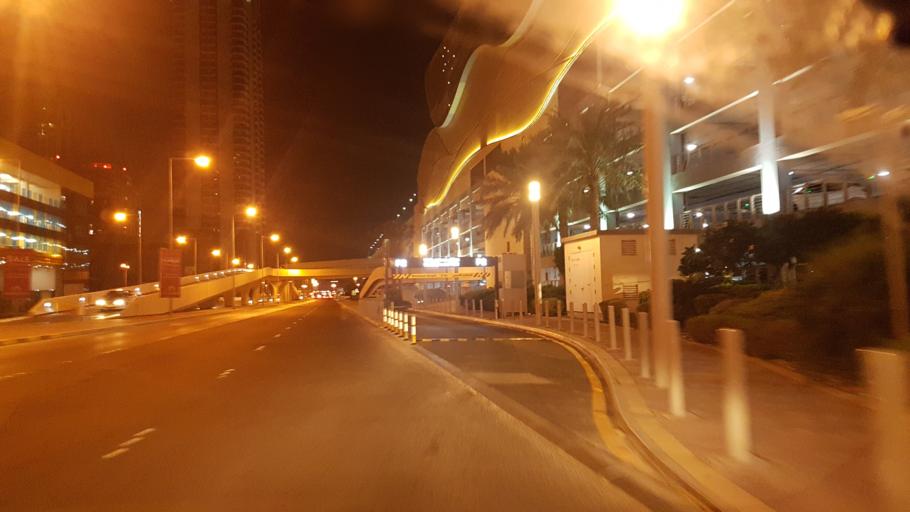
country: BH
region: Manama
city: Jidd Hafs
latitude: 26.2349
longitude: 50.5519
